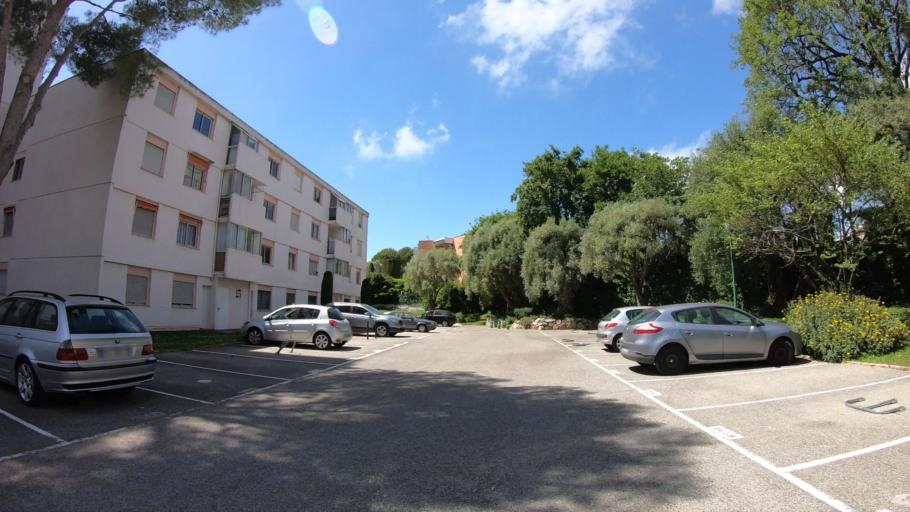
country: FR
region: Provence-Alpes-Cote d'Azur
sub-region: Departement des Alpes-Maritimes
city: Antibes
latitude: 43.5834
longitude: 7.0959
